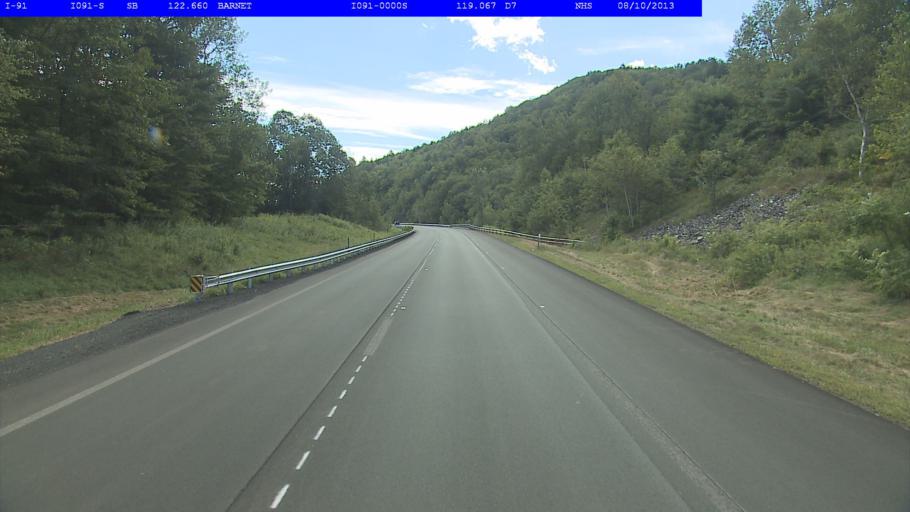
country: US
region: Vermont
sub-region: Caledonia County
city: Saint Johnsbury
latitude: 44.3198
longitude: -72.0389
